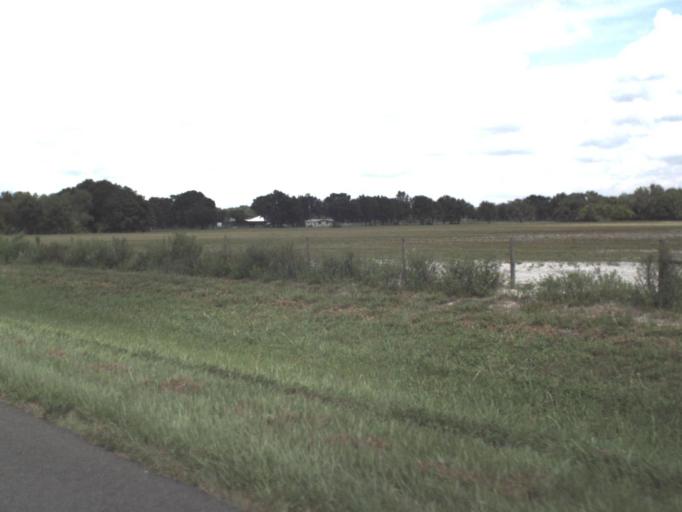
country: US
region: Florida
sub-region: Hillsborough County
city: Balm
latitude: 27.7046
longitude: -82.1754
